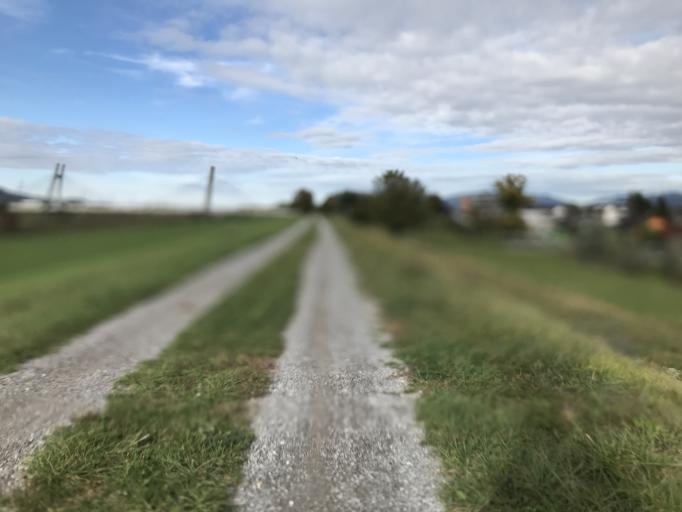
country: CH
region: Saint Gallen
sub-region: Wahlkreis Rheintal
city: Diepoldsau
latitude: 47.3868
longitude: 9.6461
